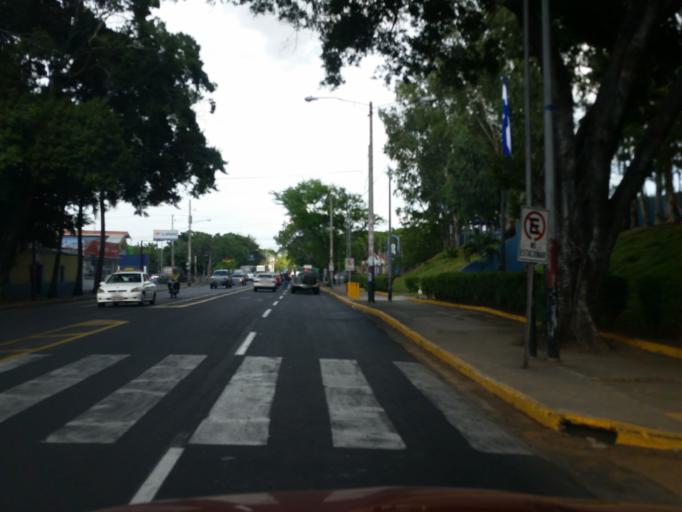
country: NI
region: Managua
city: Managua
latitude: 12.1446
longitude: -86.2695
